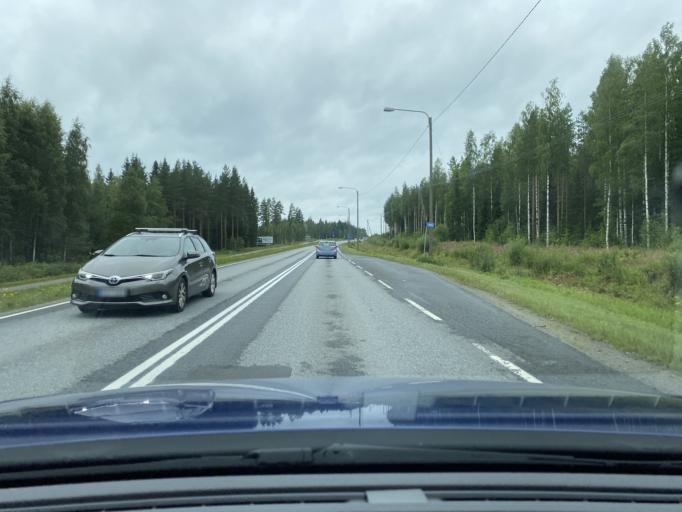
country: FI
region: Central Finland
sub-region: Keuruu
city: Keuruu
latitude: 62.2420
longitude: 24.4831
